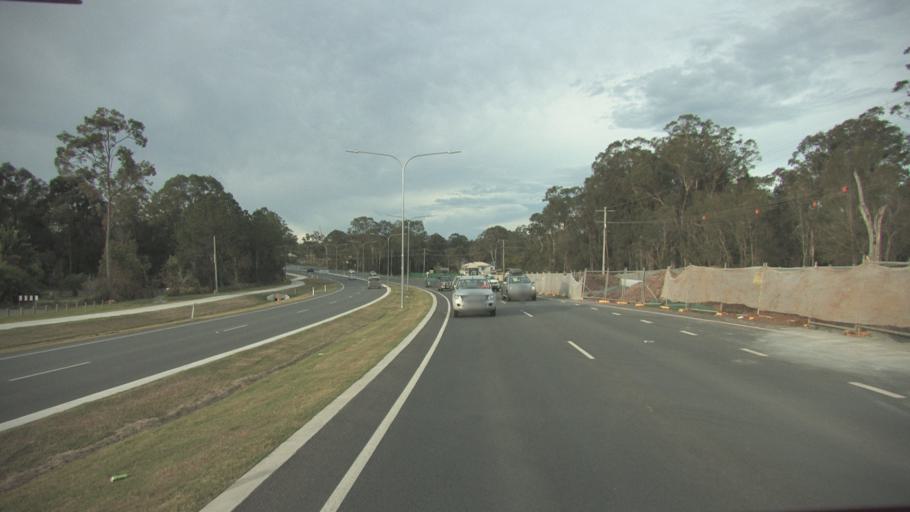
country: AU
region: Queensland
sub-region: Logan
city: Logan Reserve
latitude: -27.6966
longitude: 153.1018
